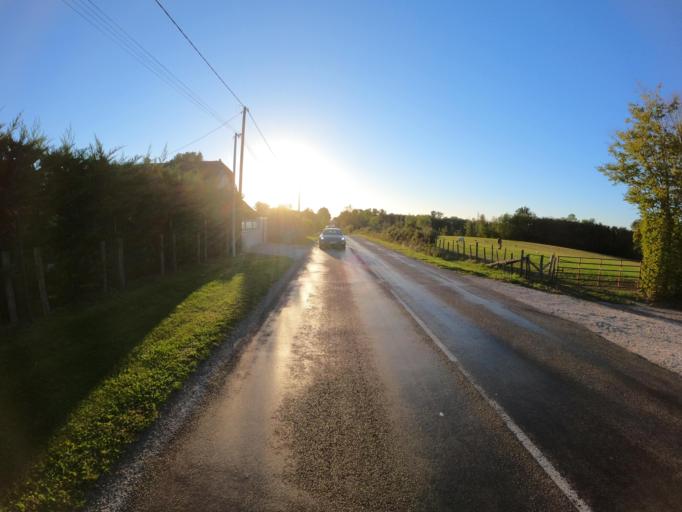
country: FR
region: Bourgogne
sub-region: Departement de Saone-et-Loire
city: Saint-Germain-du-Bois
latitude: 46.7512
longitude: 5.2647
